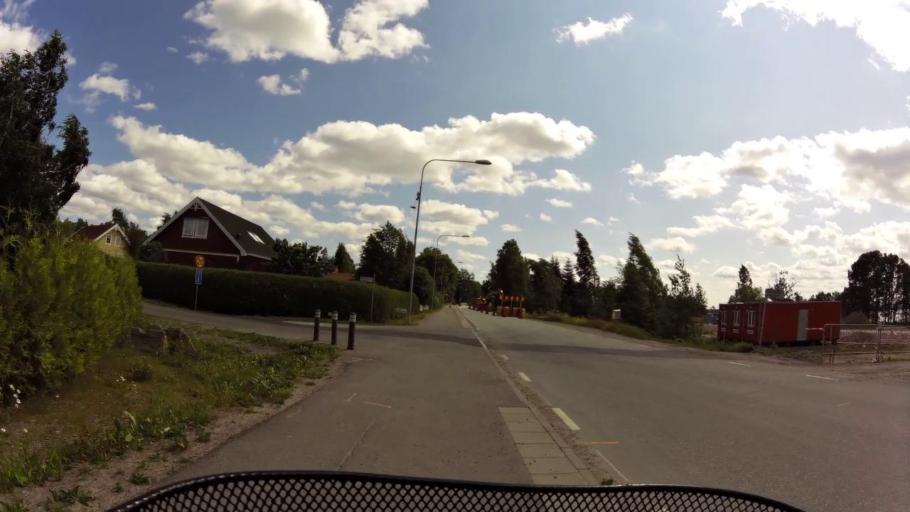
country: SE
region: OEstergoetland
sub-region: Linkopings Kommun
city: Ekangen
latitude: 58.4705
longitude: 15.6339
